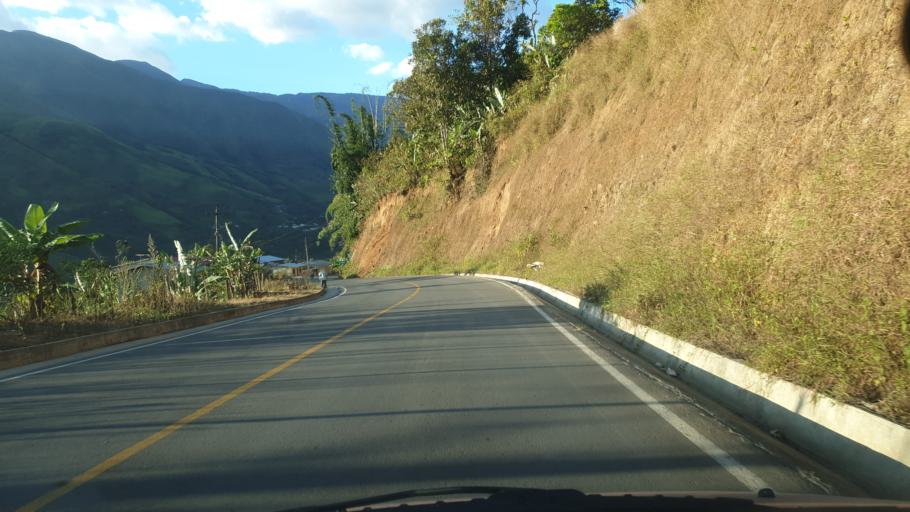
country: EC
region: El Oro
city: Zaruma
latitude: -3.6026
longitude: -79.6311
